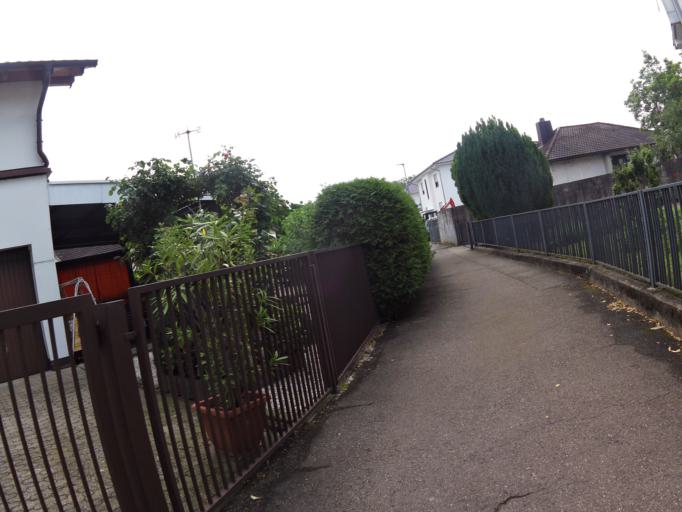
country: DE
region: Baden-Wuerttemberg
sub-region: Freiburg Region
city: Lahr
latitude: 48.3462
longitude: 7.8398
